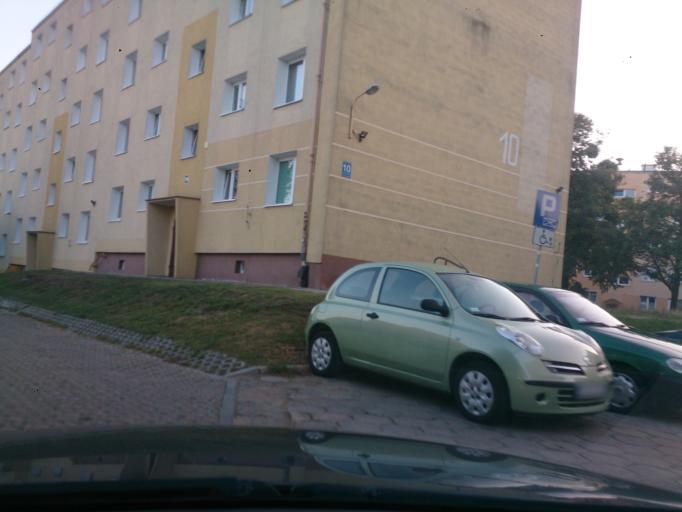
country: PL
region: Pomeranian Voivodeship
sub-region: Gdynia
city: Gdynia
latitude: 54.4919
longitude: 18.5545
